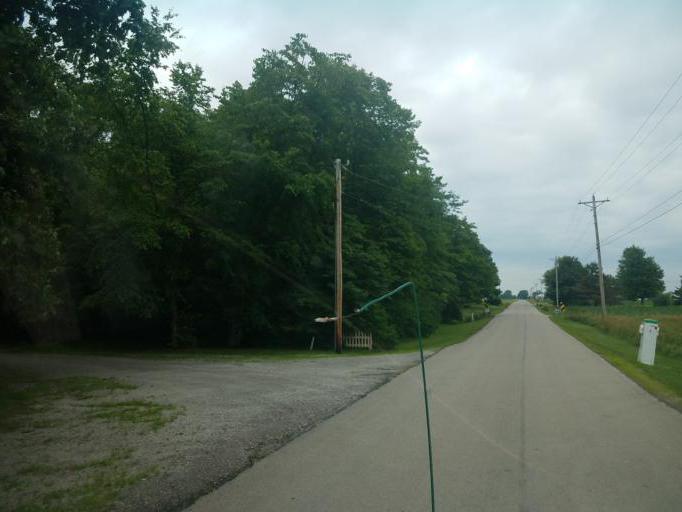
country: US
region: Ohio
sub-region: Hardin County
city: Ada
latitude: 40.7912
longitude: -83.8365
